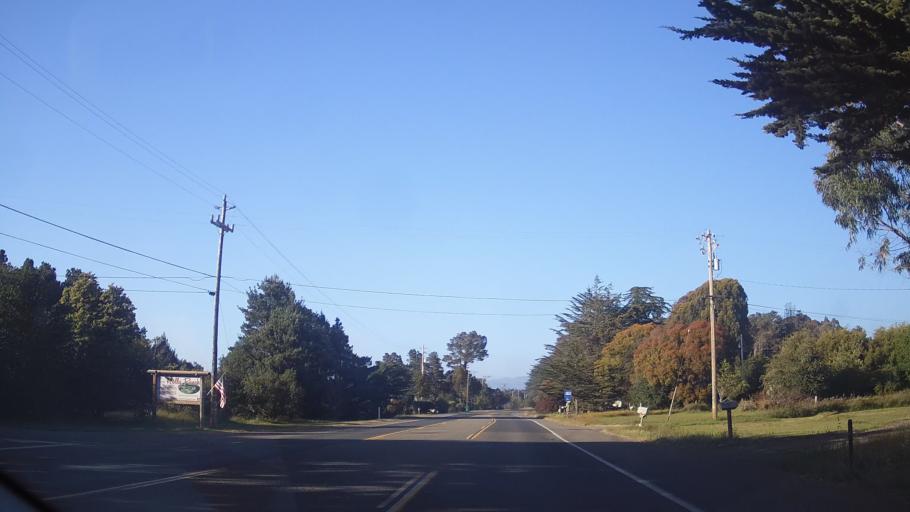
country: US
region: California
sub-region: Mendocino County
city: Fort Bragg
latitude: 39.4813
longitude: -123.7946
